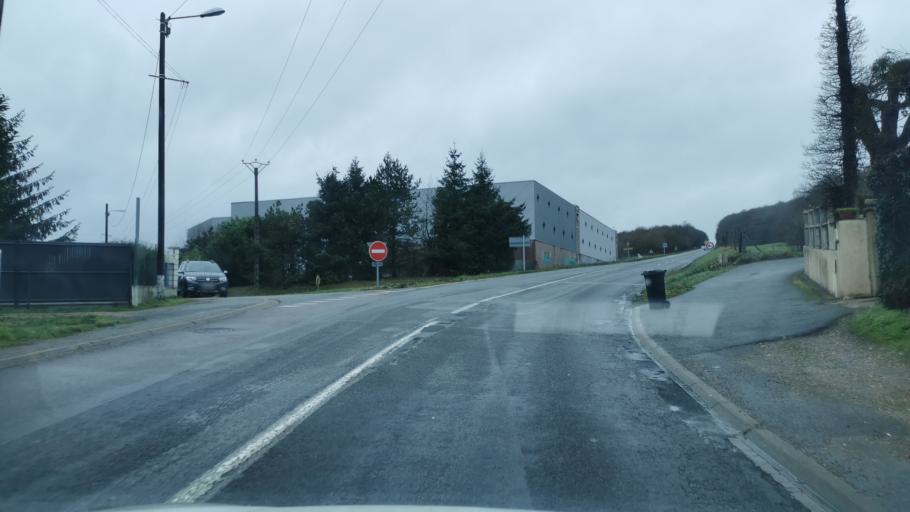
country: FR
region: Haute-Normandie
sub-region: Departement de l'Eure
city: Gravigny
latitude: 49.0681
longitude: 1.1729
